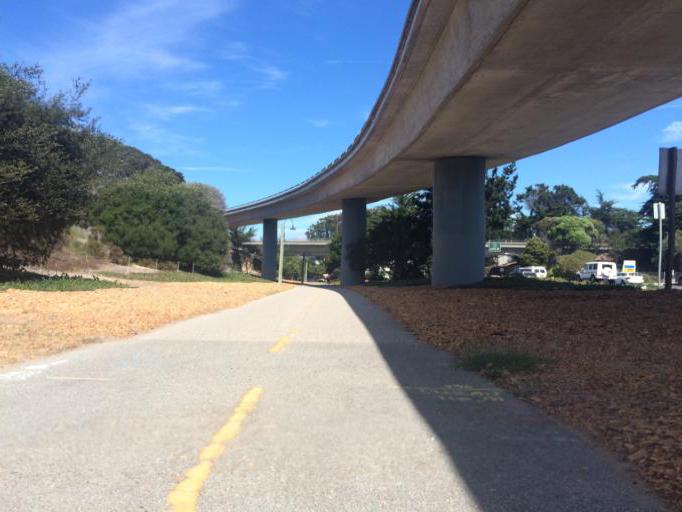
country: US
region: California
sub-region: Monterey County
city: Seaside
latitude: 36.6040
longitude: -121.8626
